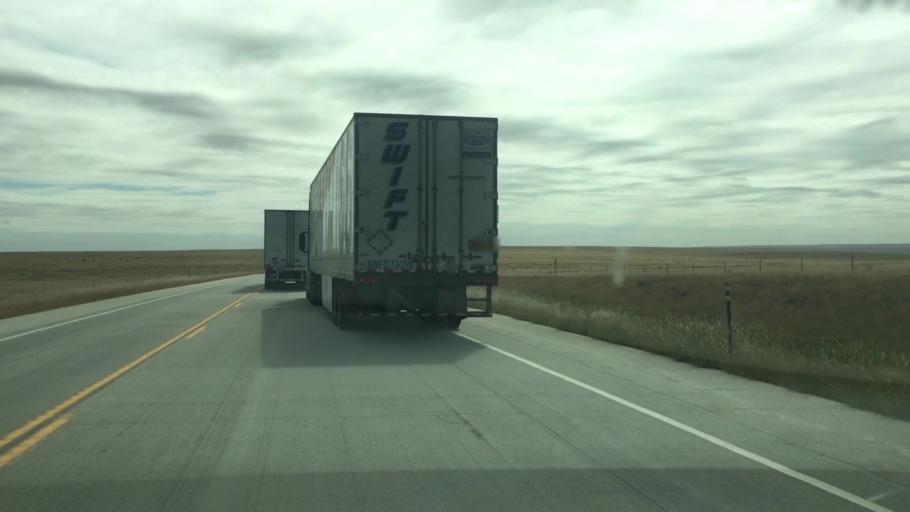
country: US
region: Colorado
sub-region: Lincoln County
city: Hugo
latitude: 38.9744
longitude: -103.2531
